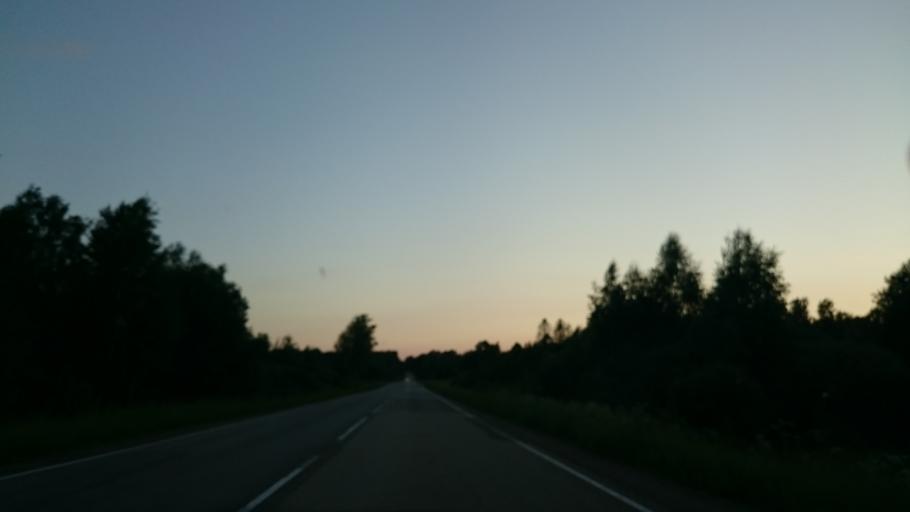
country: LV
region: Ludzas Rajons
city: Ludza
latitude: 56.5342
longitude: 27.6029
